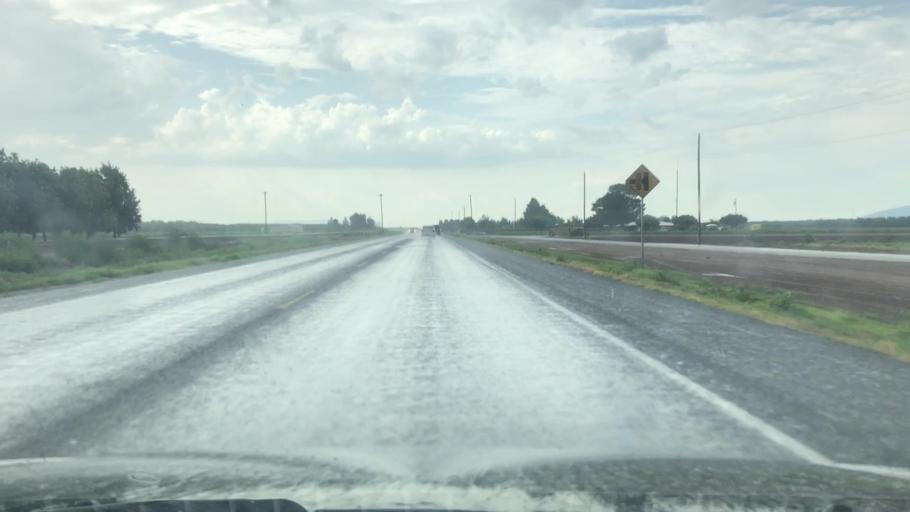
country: US
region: New Mexico
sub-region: Dona Ana County
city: Mesquite
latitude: 32.1721
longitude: -106.7013
